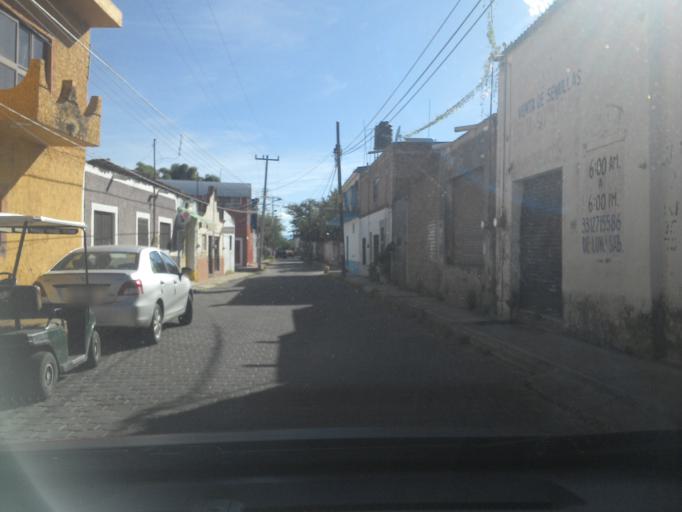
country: MX
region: Jalisco
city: Teuchitlan
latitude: 20.6829
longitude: -103.8472
